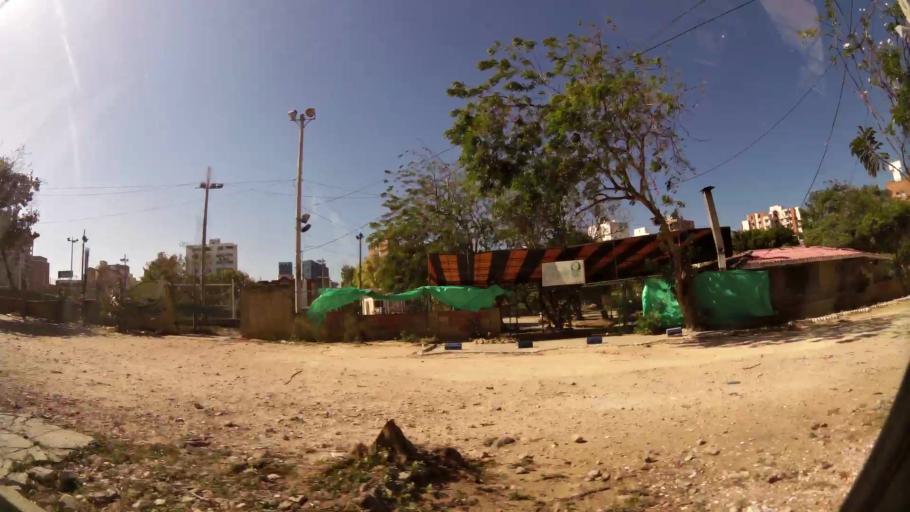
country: CO
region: Atlantico
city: Barranquilla
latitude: 11.0136
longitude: -74.8224
